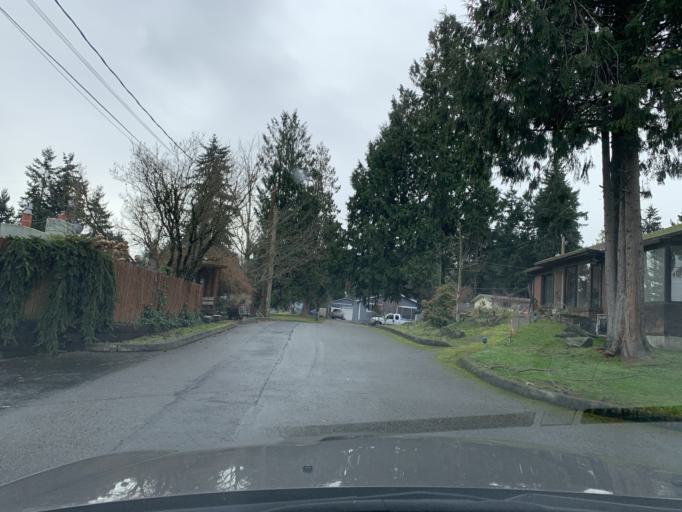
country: US
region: Washington
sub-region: King County
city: Tukwila
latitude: 47.4637
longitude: -122.2768
